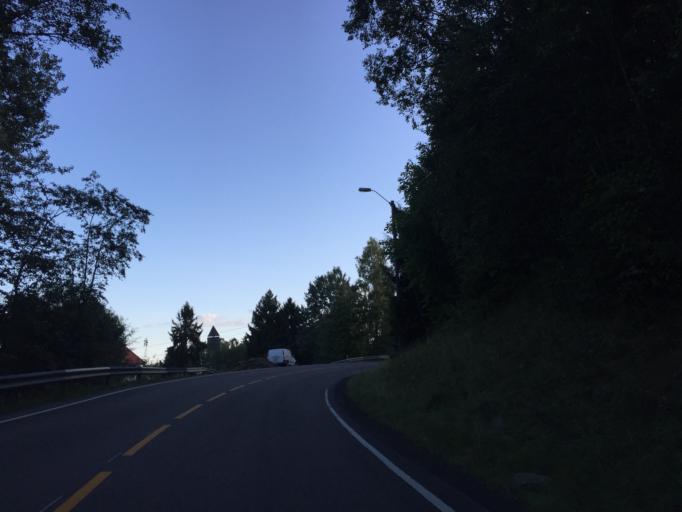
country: NO
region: Akershus
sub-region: Fet
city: Fetsund
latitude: 59.8856
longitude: 11.2107
